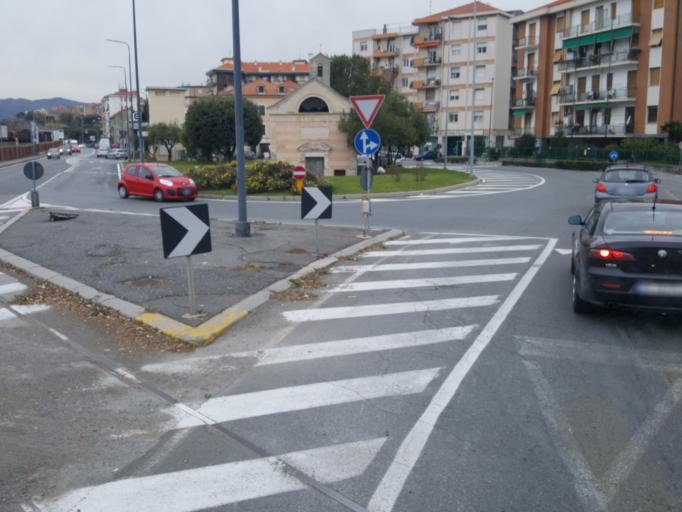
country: IT
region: Liguria
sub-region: Provincia di Savona
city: Savona
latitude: 44.2964
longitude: 8.4573
